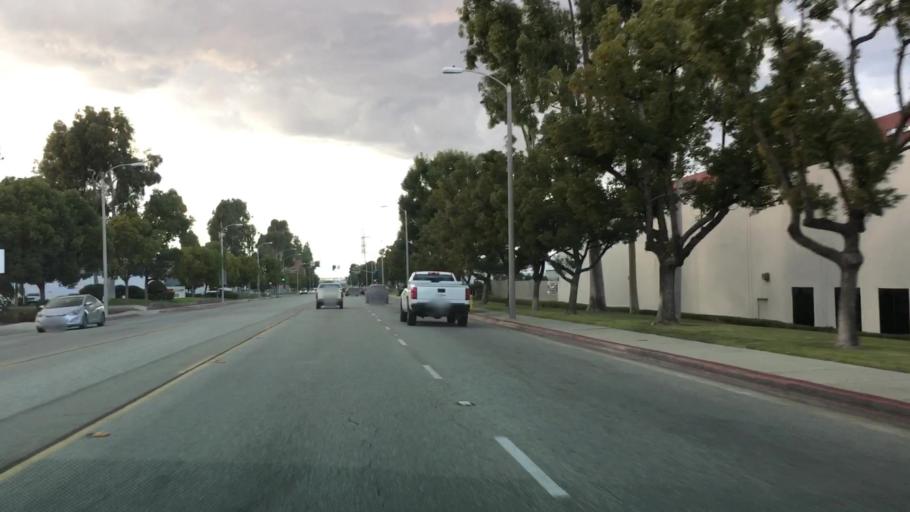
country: US
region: California
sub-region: Los Angeles County
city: La Puente
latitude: 34.0038
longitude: -117.9426
